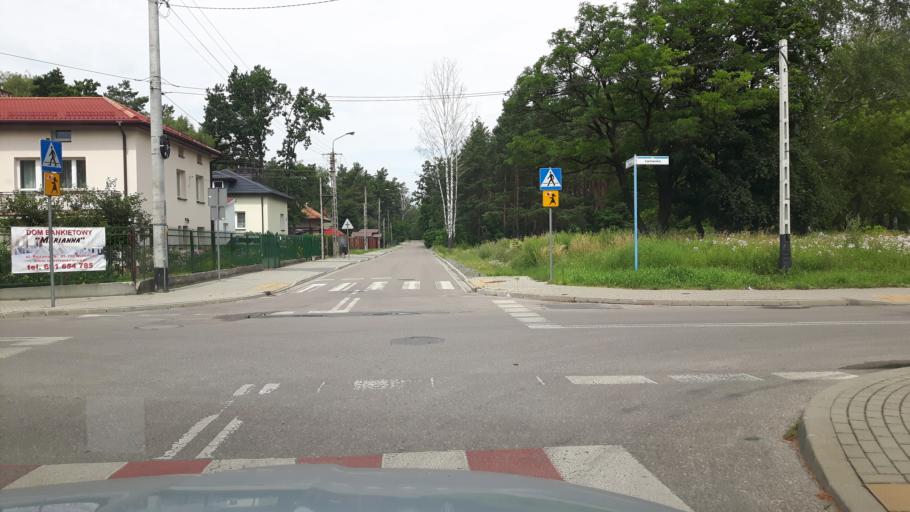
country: PL
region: Masovian Voivodeship
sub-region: Powiat wolominski
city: Wolomin
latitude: 52.3499
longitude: 21.2244
